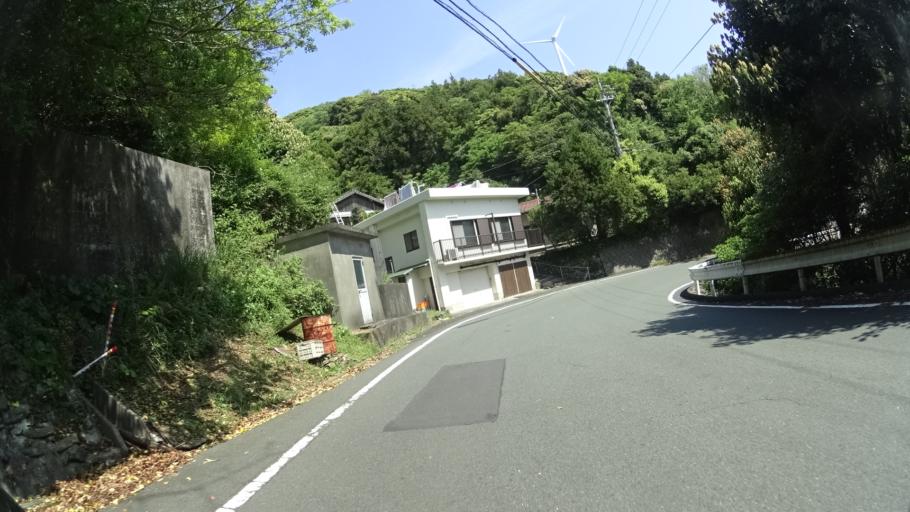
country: JP
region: Ehime
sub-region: Nishiuwa-gun
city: Ikata-cho
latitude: 33.3829
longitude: 132.0852
